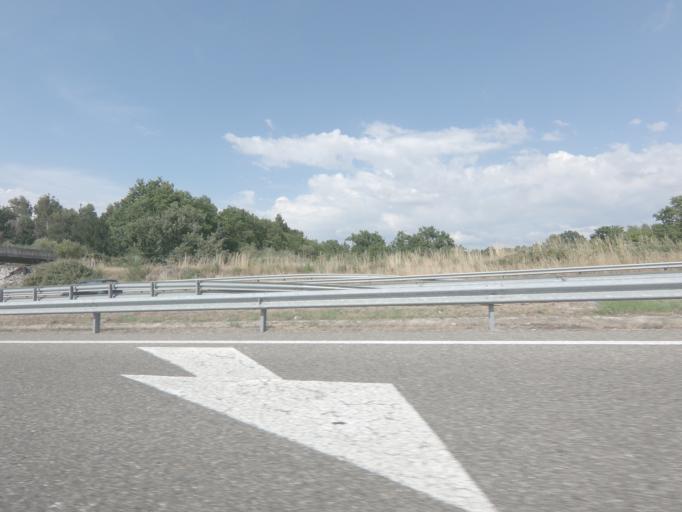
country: ES
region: Galicia
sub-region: Provincia de Ourense
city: Taboadela
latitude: 42.2666
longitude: -7.8700
